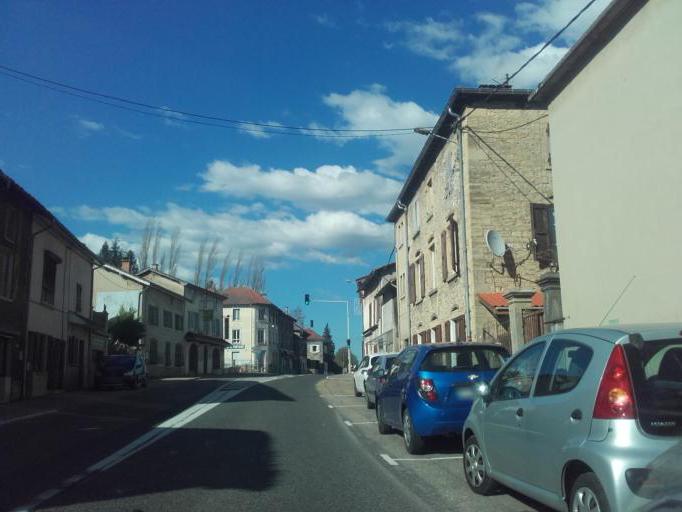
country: FR
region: Rhone-Alpes
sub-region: Departement de l'Isere
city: Nivolas-Vermelle
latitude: 45.5322
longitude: 5.3082
